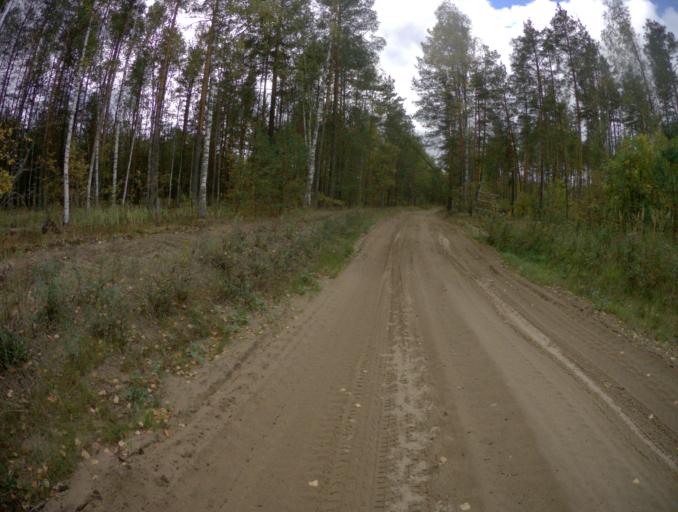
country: RU
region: Vladimir
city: Petushki
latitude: 55.8651
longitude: 39.5387
